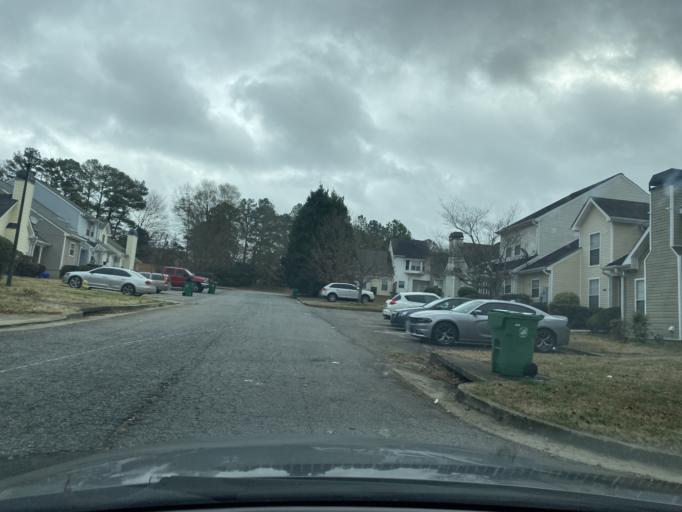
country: US
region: Georgia
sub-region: DeKalb County
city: Pine Mountain
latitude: 33.6973
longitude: -84.1473
